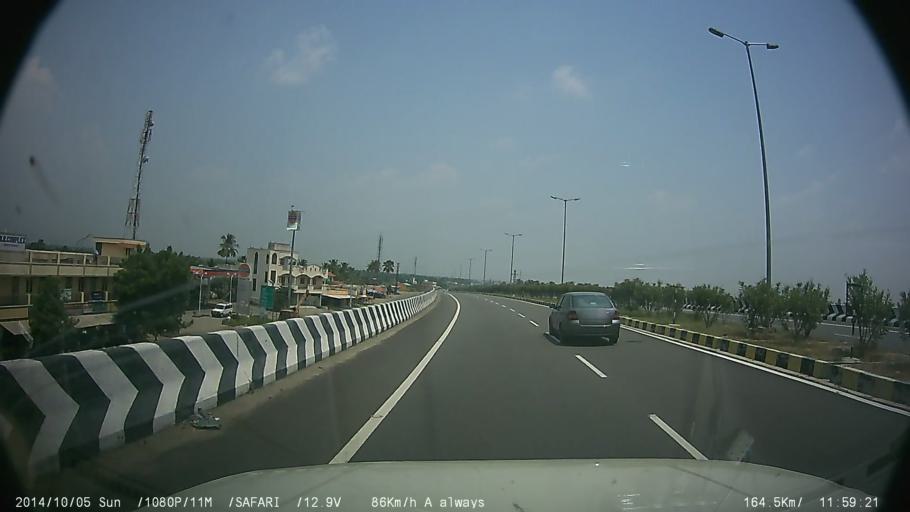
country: IN
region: Tamil Nadu
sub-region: Villupuram
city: Chinna Salem
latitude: 11.5931
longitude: 78.8074
